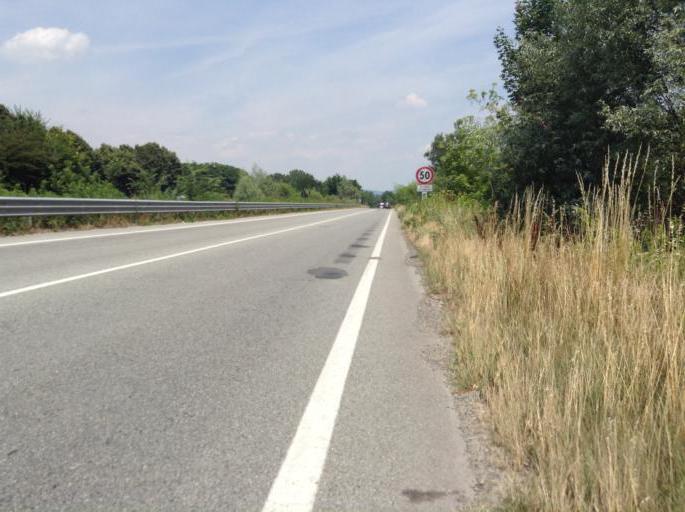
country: IT
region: Piedmont
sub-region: Provincia di Torino
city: Carignano
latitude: 44.9066
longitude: 7.6788
